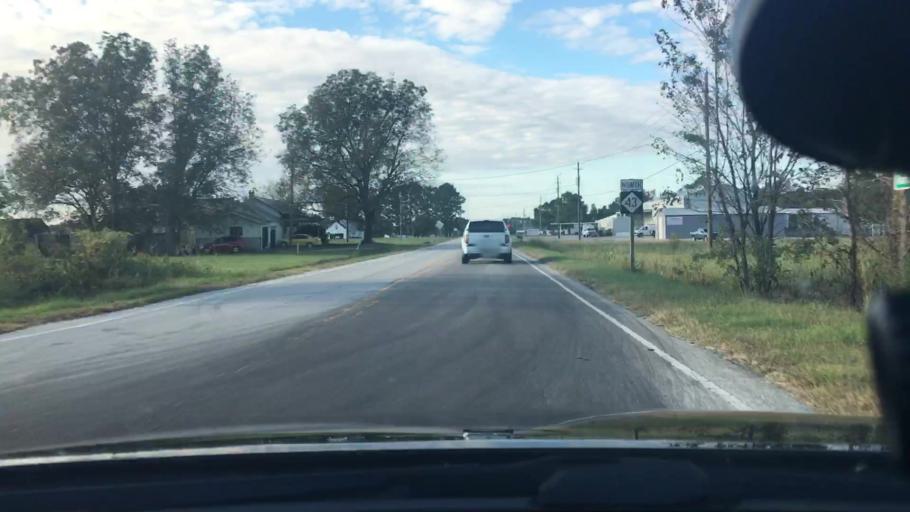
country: US
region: North Carolina
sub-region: Pitt County
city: Windsor
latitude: 35.4940
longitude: -77.3084
